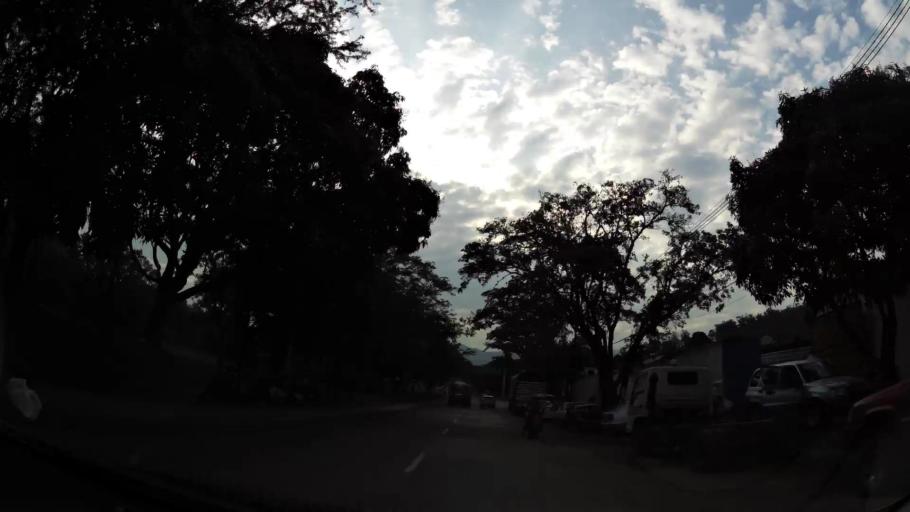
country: CO
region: Antioquia
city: Medellin
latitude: 6.2593
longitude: -75.5775
